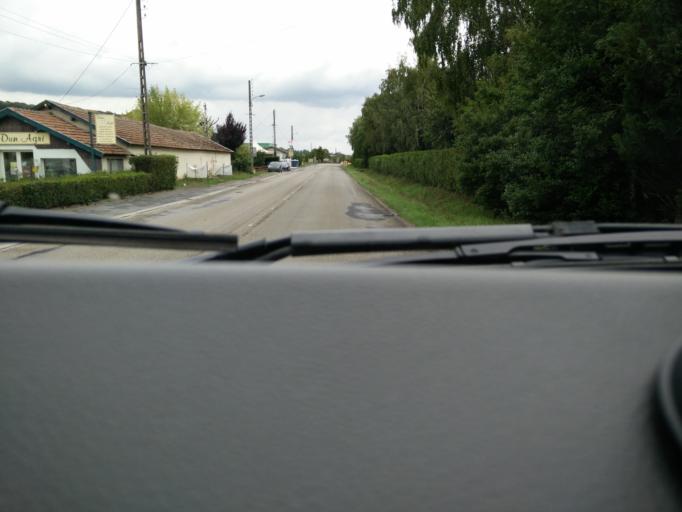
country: FR
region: Lorraine
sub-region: Departement de la Meuse
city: Stenay
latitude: 49.3902
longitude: 5.1826
